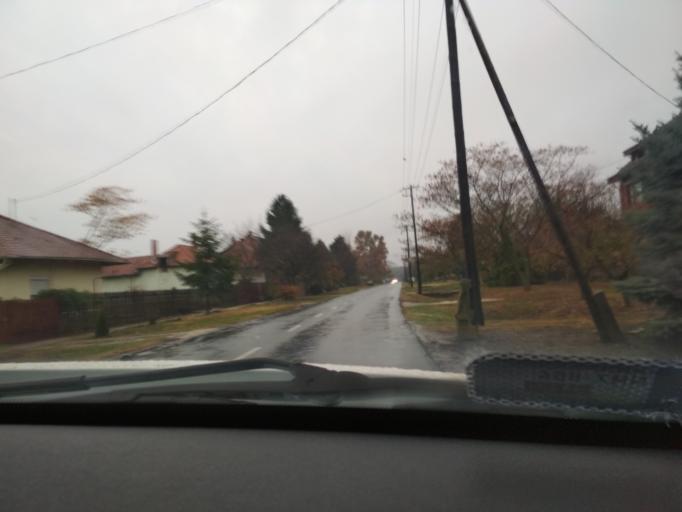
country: HU
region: Csongrad
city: Baks
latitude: 46.5428
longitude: 20.1034
